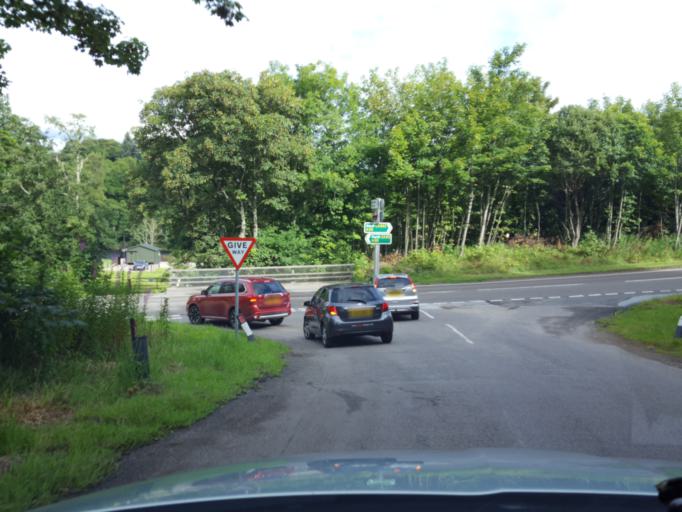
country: GB
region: Scotland
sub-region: Moray
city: Rothes
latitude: 57.4798
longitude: -3.2007
